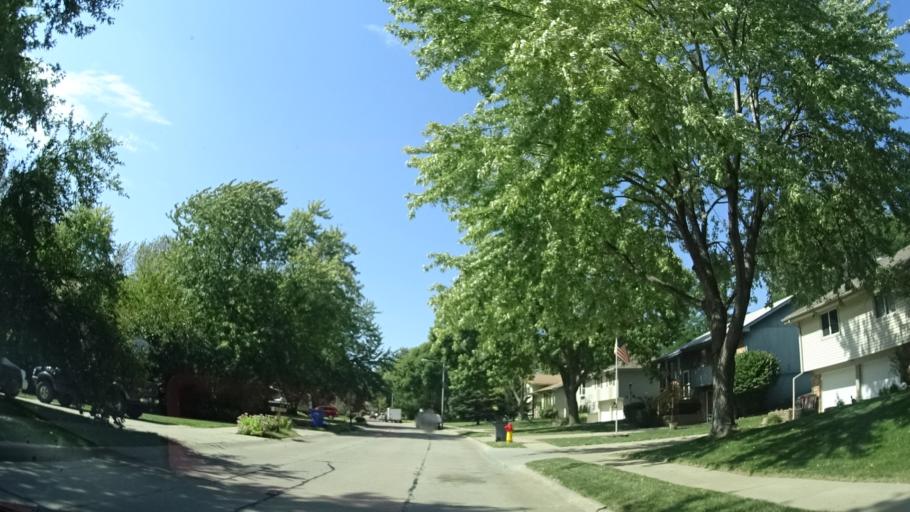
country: US
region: Nebraska
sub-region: Sarpy County
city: Offutt Air Force Base
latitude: 41.1314
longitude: -95.9526
